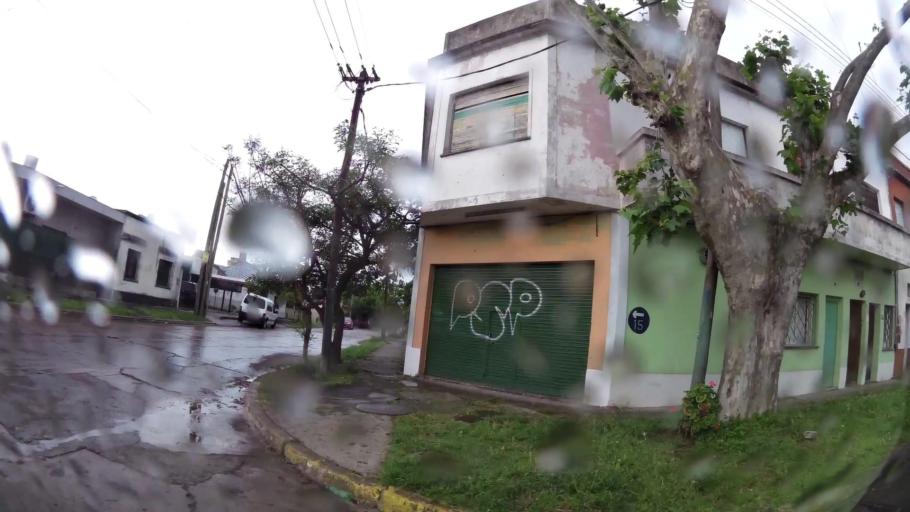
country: AR
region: Buenos Aires
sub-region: Partido de Quilmes
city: Quilmes
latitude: -34.7699
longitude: -58.2220
